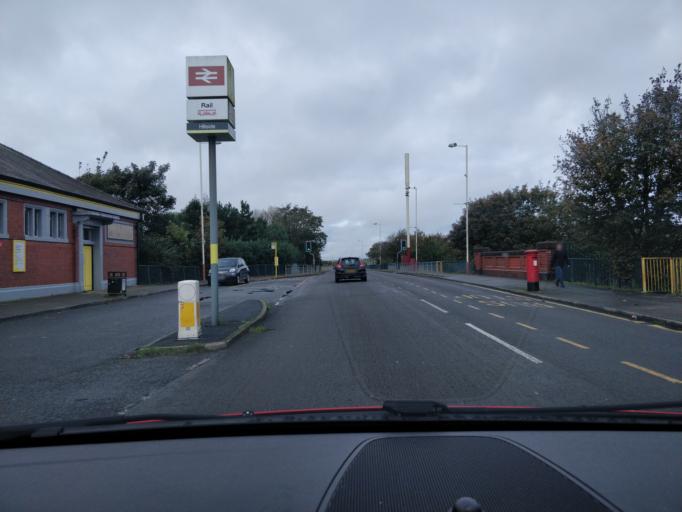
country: GB
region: England
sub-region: Sefton
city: Southport
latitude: 53.6220
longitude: -3.0245
